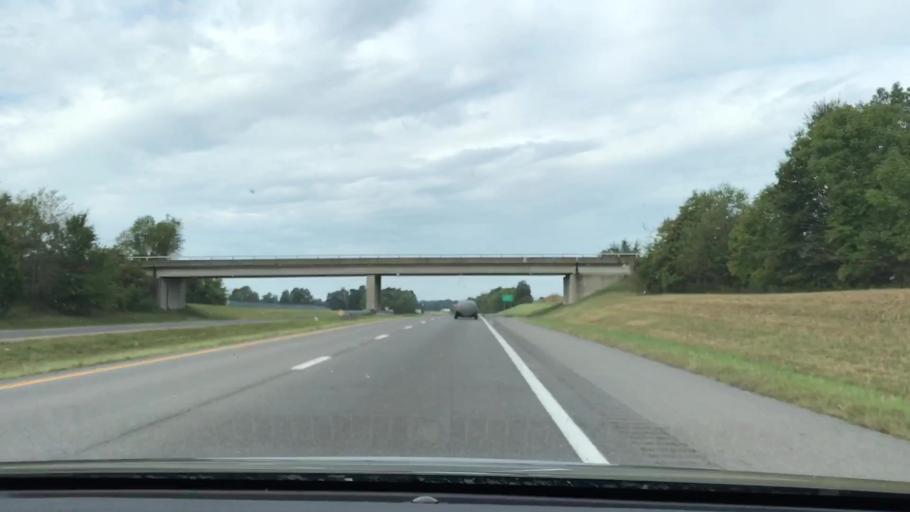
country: US
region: Kentucky
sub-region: Graves County
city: Mayfield
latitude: 36.7782
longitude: -88.5812
